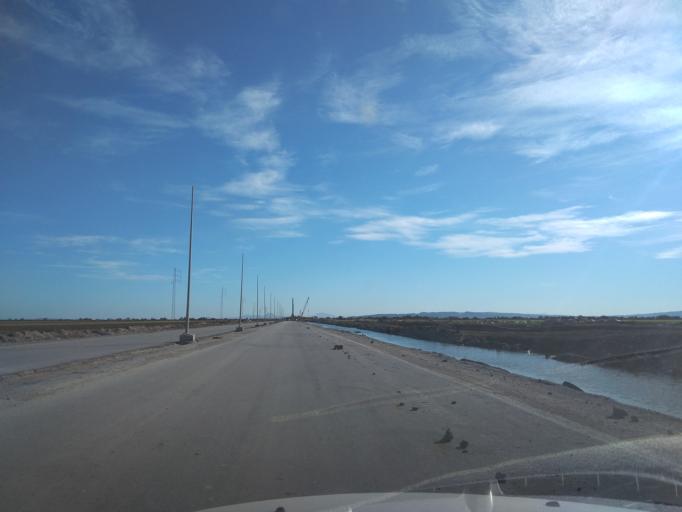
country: TN
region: Ariana
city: Qal'at al Andalus
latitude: 37.0293
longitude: 10.1373
